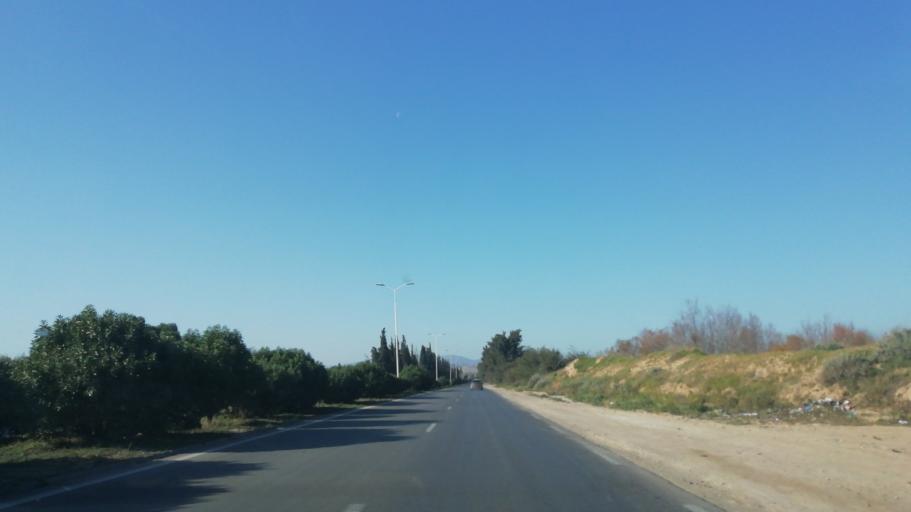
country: DZ
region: Mascara
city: Mascara
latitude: 35.6052
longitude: 0.0901
